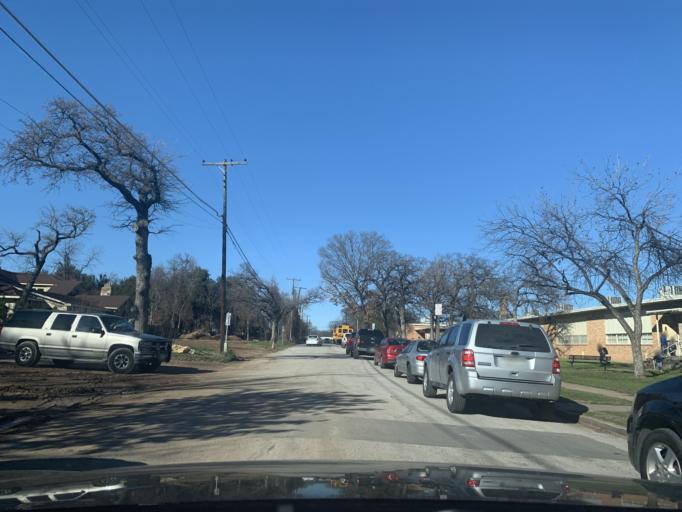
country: US
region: Texas
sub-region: Tarrant County
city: Haltom City
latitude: 32.7799
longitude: -97.2874
